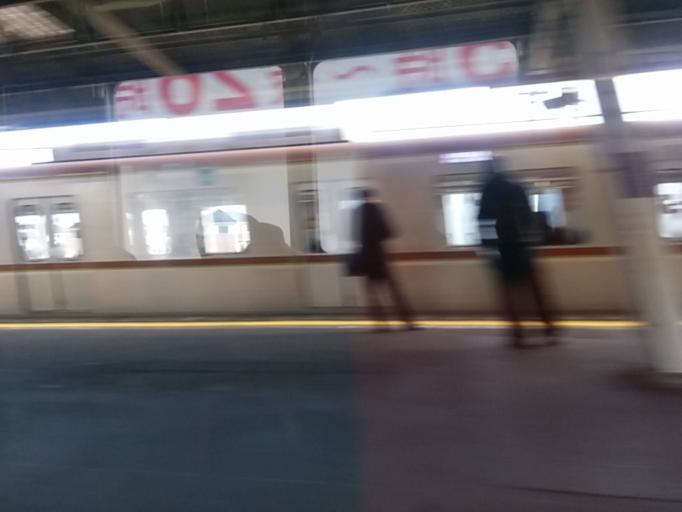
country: JP
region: Saitama
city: Kawagoe
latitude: 35.8910
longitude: 139.4971
